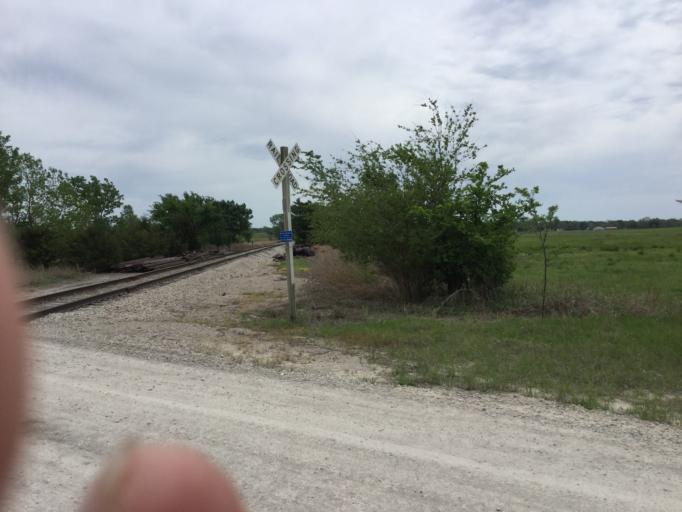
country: US
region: Kansas
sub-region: Montgomery County
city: Cherryvale
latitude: 37.2818
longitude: -95.5643
